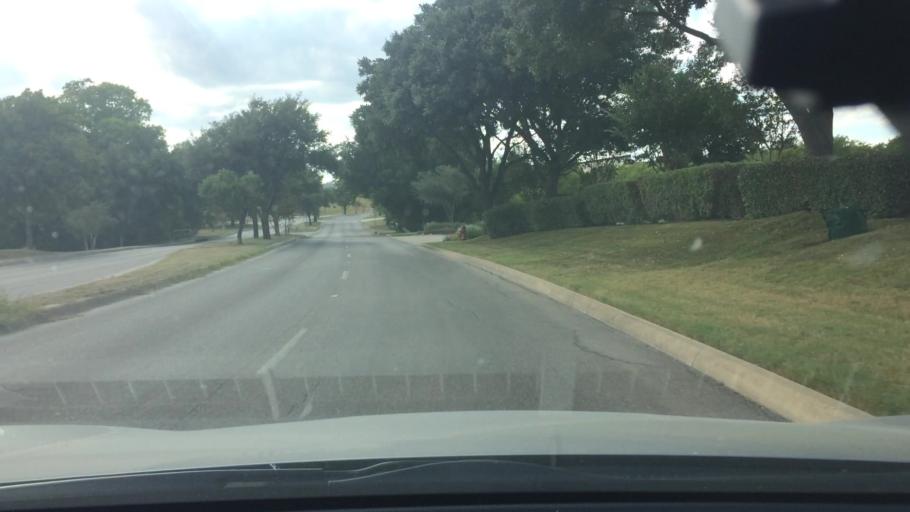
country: US
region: Texas
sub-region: Bexar County
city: Universal City
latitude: 29.5453
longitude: -98.3037
